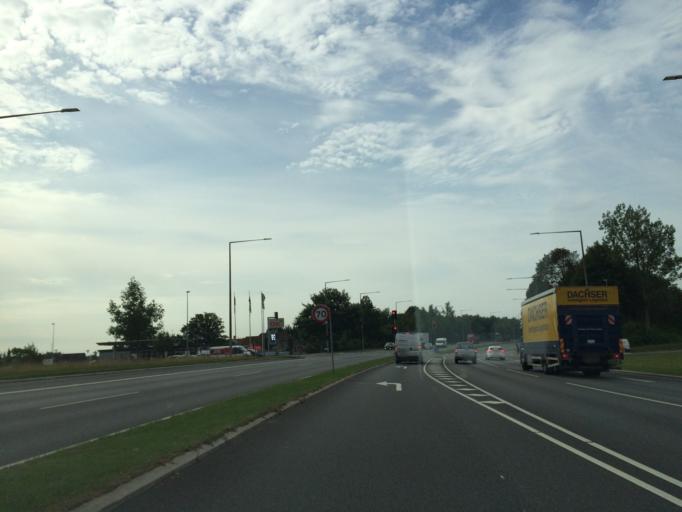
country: DK
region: South Denmark
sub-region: Kolding Kommune
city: Kolding
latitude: 55.5078
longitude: 9.5047
